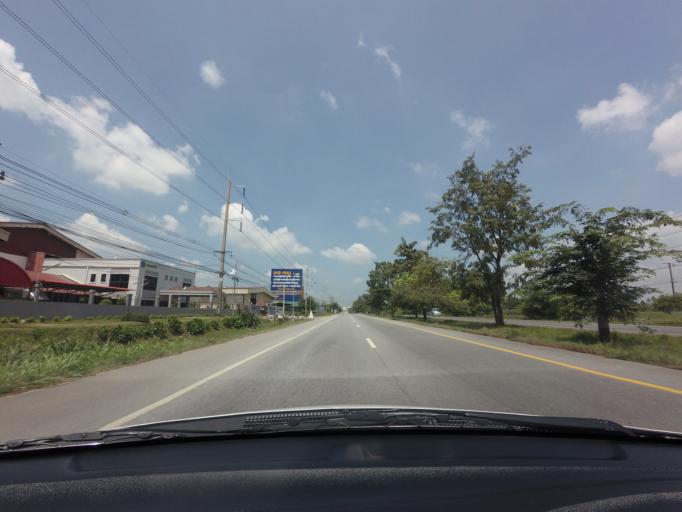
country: TH
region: Prachin Buri
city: Si Maha Phot
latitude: 13.8362
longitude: 101.5515
